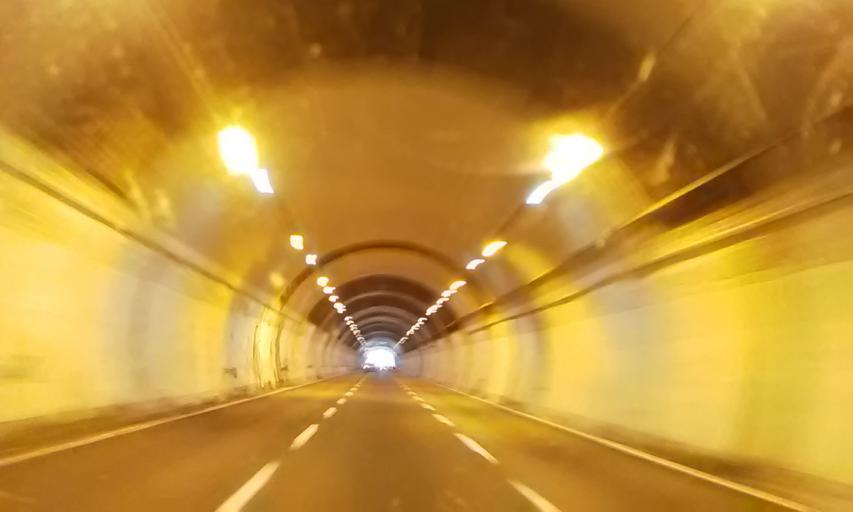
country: IT
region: Liguria
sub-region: Provincia di Genova
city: Mele
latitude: 44.4233
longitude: 8.7327
